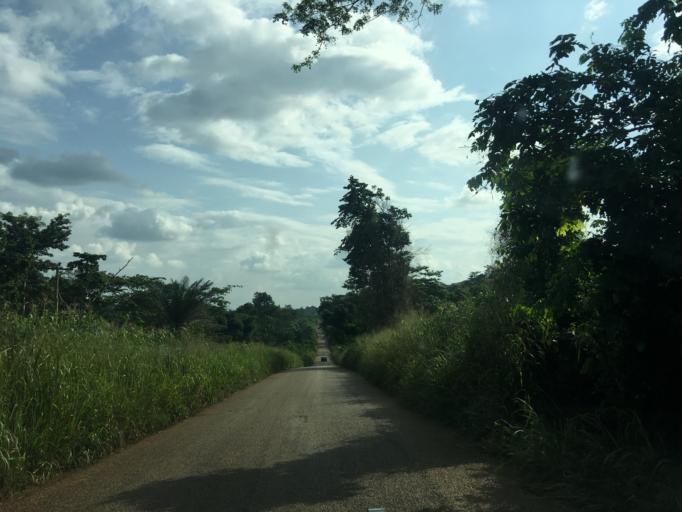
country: GH
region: Western
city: Bibiani
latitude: 6.7690
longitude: -2.5713
